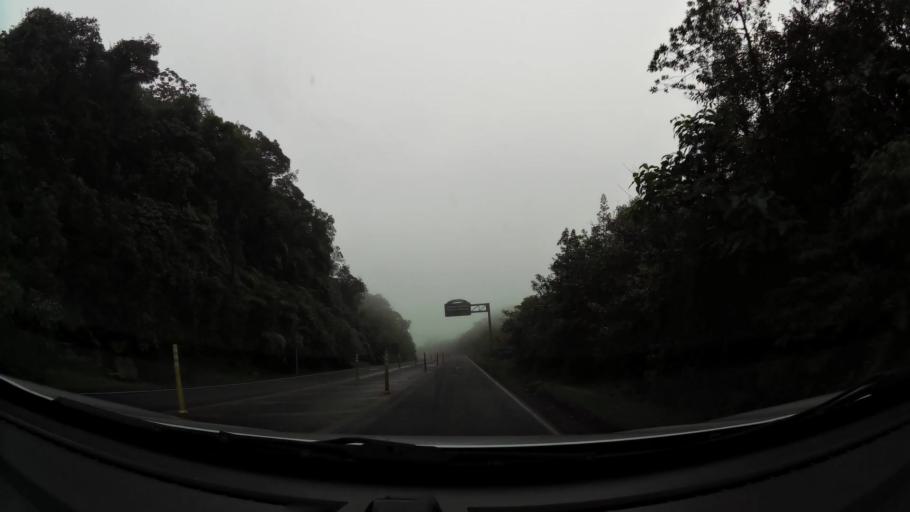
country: CR
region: Heredia
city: Angeles
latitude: 10.0511
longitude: -84.0050
